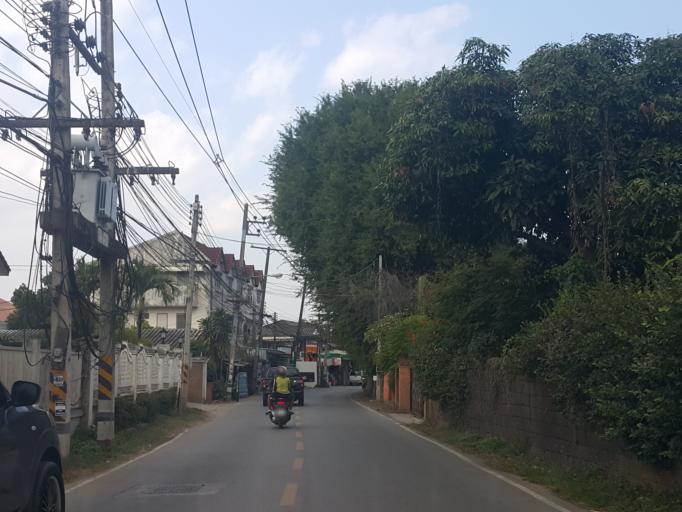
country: TH
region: Chiang Mai
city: Chiang Mai
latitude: 18.8352
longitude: 98.9900
